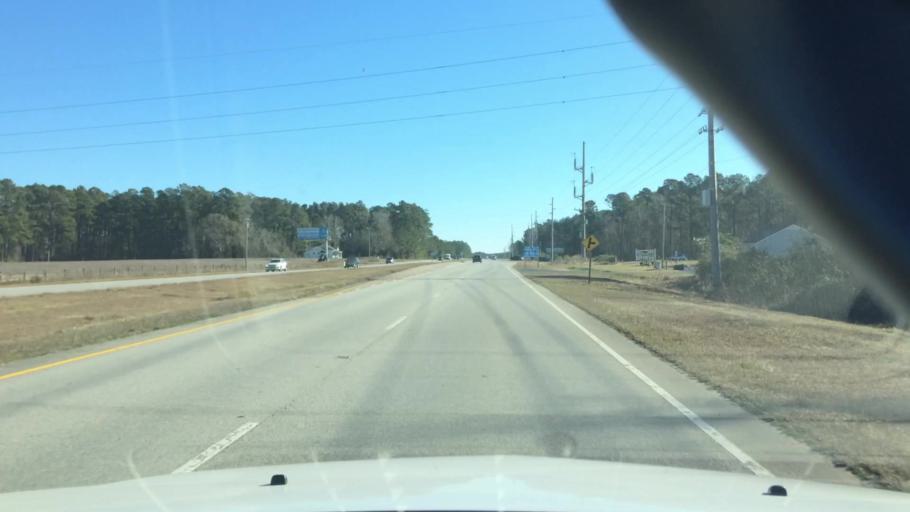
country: US
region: North Carolina
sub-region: Brunswick County
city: Shallotte
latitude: 33.9541
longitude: -78.4509
